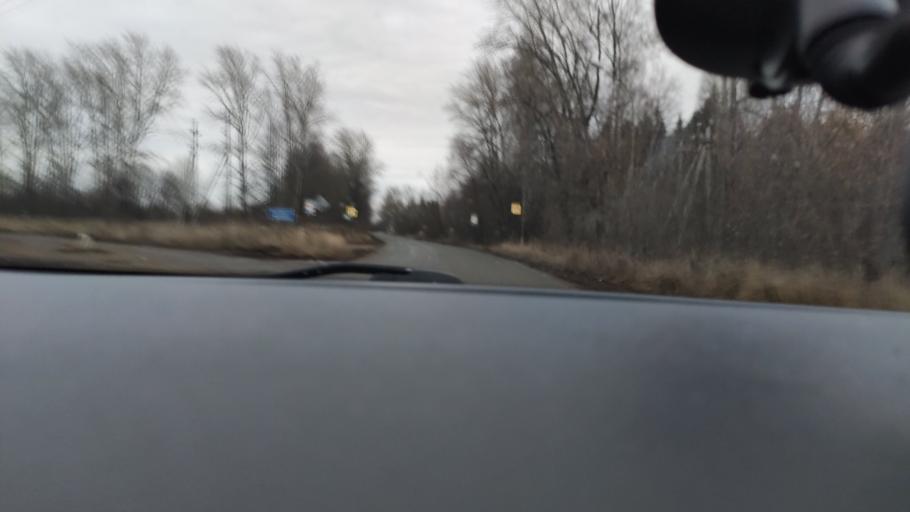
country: RU
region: Perm
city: Perm
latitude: 57.9621
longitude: 56.1971
